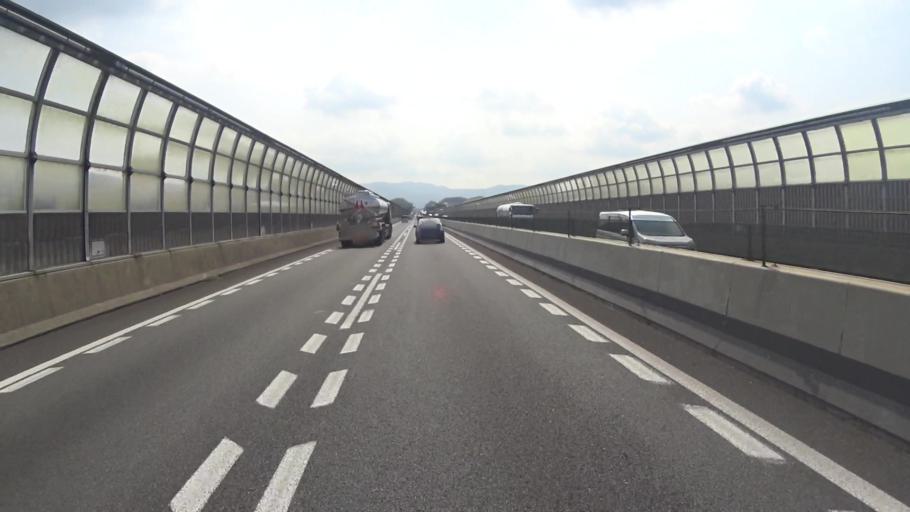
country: JP
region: Kyoto
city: Kyoto
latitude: 34.9567
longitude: 135.7721
